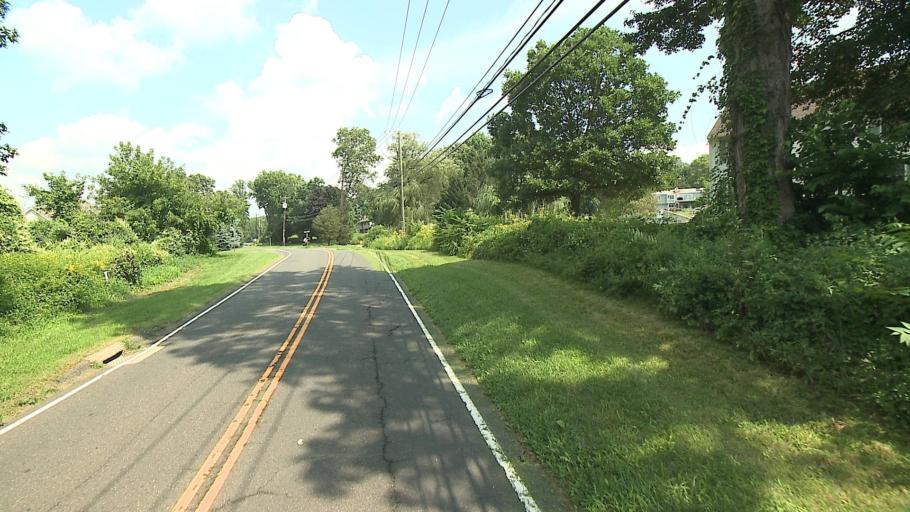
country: US
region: Connecticut
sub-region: Litchfield County
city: New Milford
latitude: 41.6133
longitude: -73.3867
